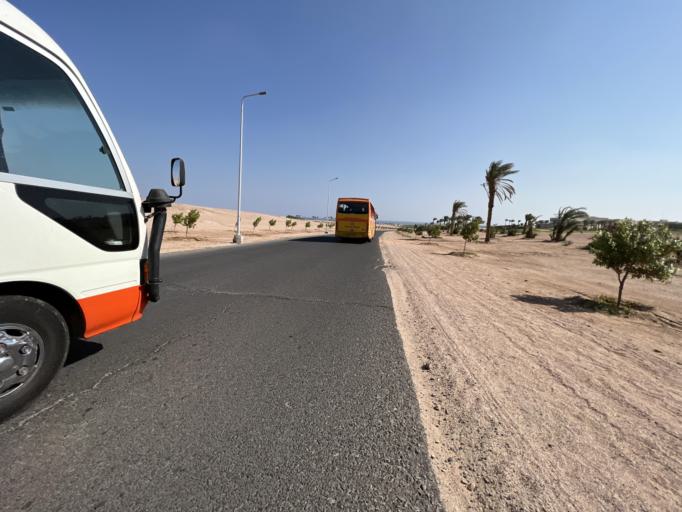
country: EG
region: Red Sea
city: Makadi Bay
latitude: 26.9854
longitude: 33.8842
